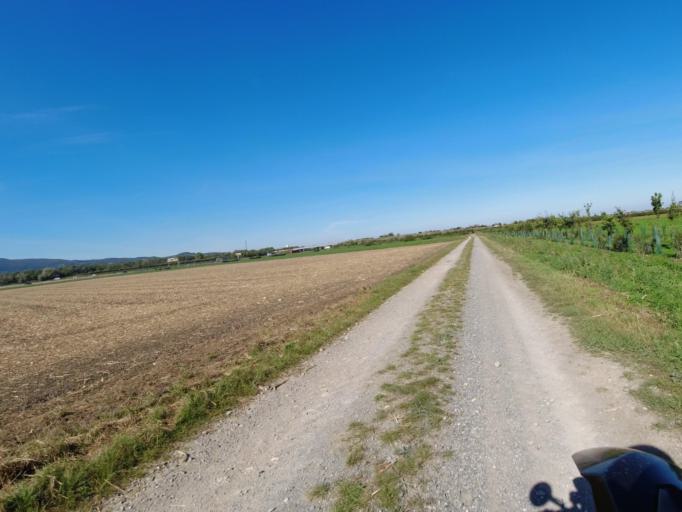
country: AT
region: Lower Austria
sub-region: Politischer Bezirk Baden
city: Trumau
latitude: 48.0249
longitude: 16.3389
